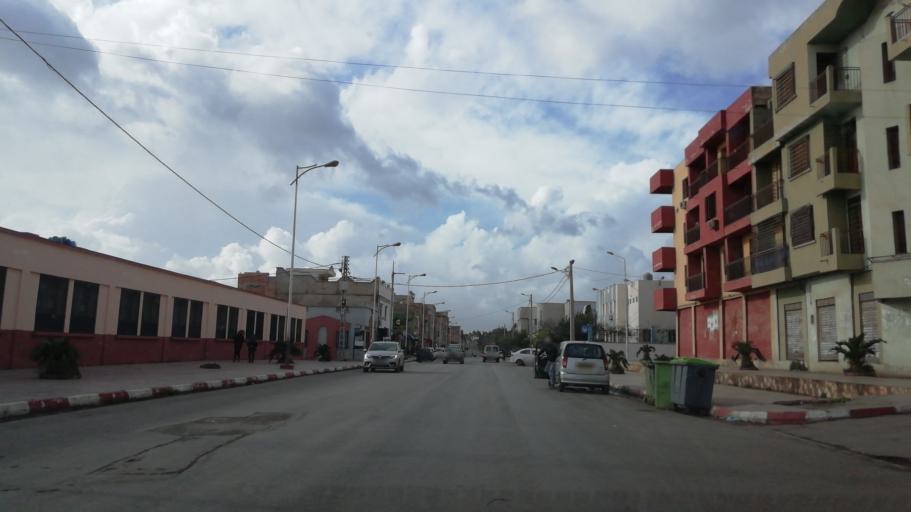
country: DZ
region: Oran
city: Oran
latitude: 35.6808
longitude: -0.6179
